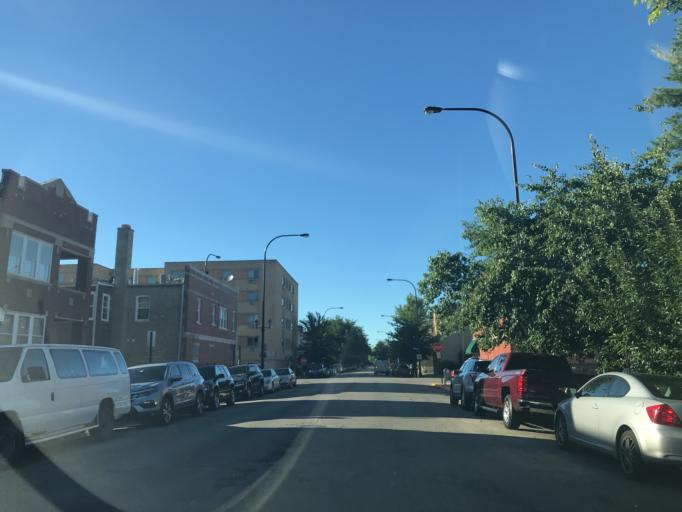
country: US
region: Illinois
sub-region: Cook County
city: Cicero
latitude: 41.8613
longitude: -87.7495
